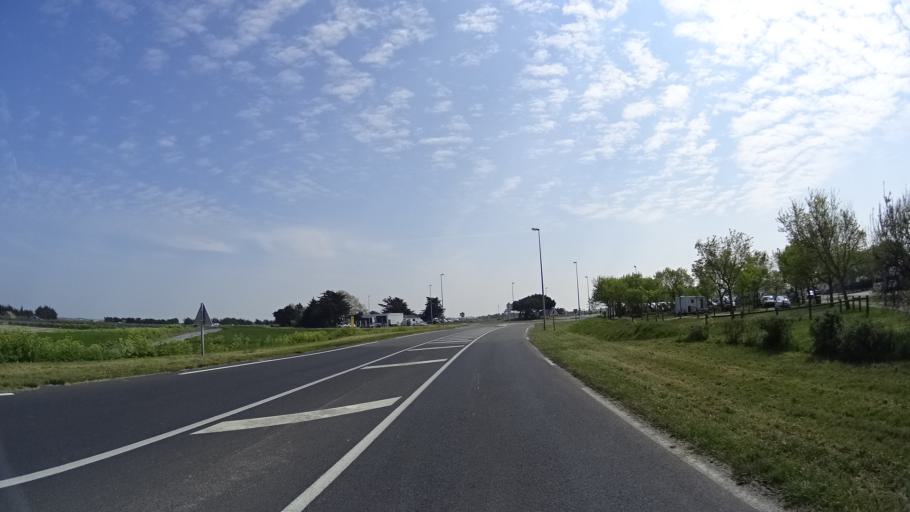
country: FR
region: Pays de la Loire
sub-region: Departement de la Vendee
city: La Gueriniere
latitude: 46.9824
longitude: -2.2647
